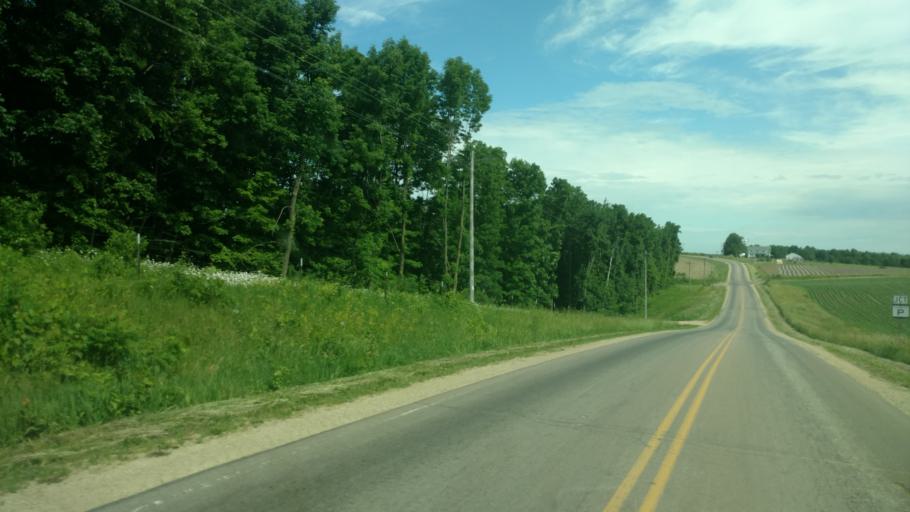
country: US
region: Wisconsin
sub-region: Vernon County
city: Hillsboro
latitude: 43.6435
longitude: -90.4525
